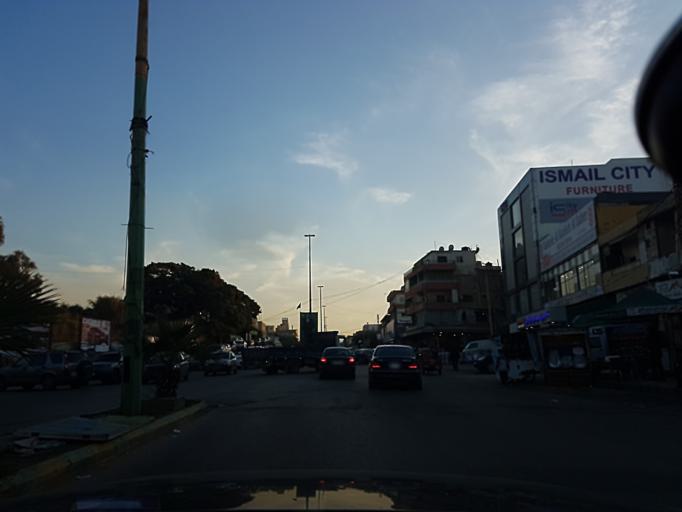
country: LB
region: Beyrouth
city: Beirut
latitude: 33.8521
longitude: 35.4852
